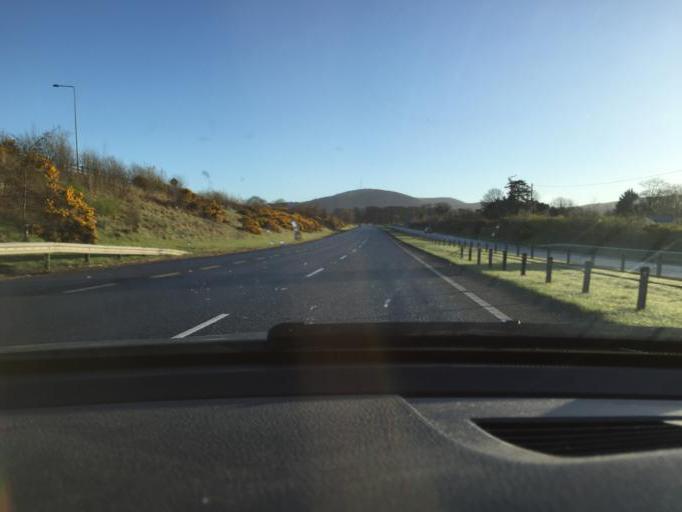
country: IE
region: Leinster
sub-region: Lu
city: Dundalk
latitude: 54.0450
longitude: -6.3664
